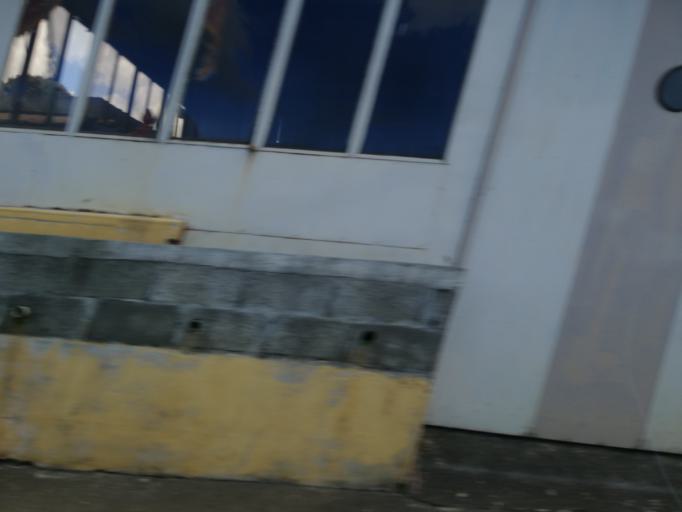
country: MU
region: Flacq
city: Camp de Masque
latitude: -20.2354
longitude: 57.6805
